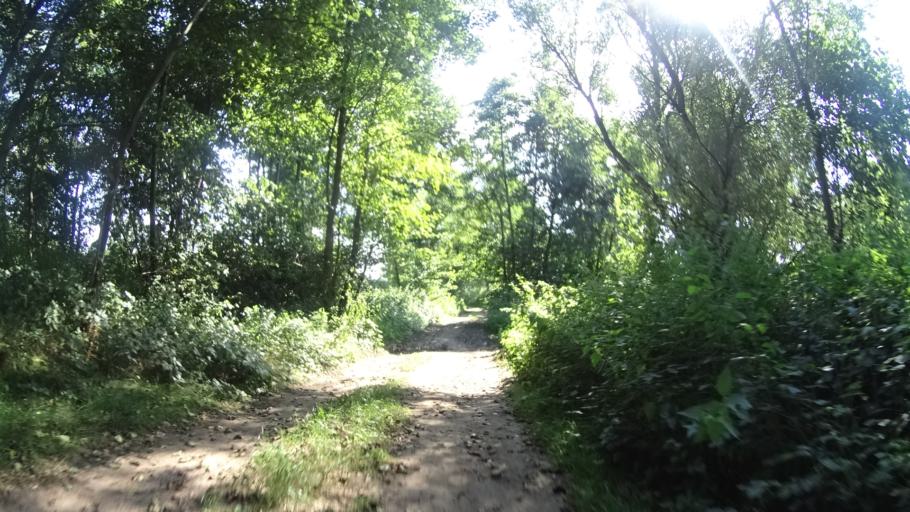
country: PL
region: Masovian Voivodeship
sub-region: Powiat bialobrzeski
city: Wysmierzyce
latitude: 51.6390
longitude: 20.8186
